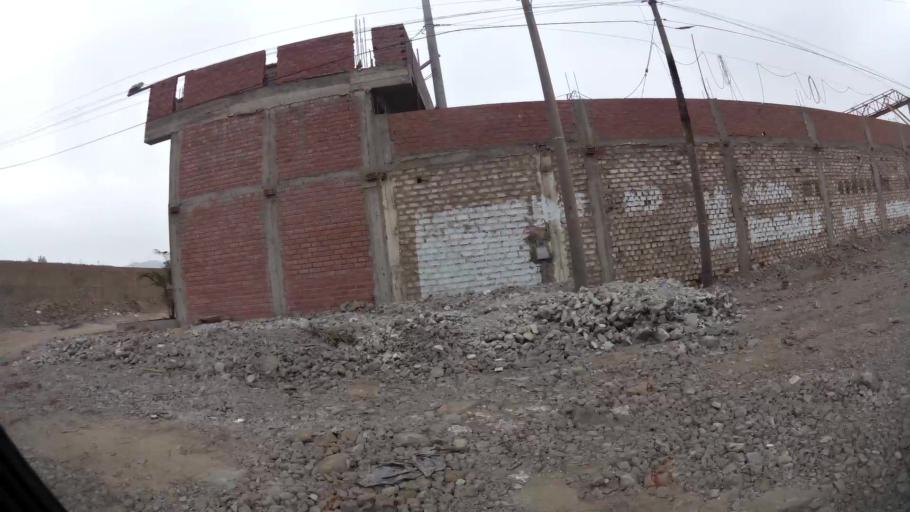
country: PE
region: Lima
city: Ventanilla
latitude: -11.8401
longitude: -77.1154
